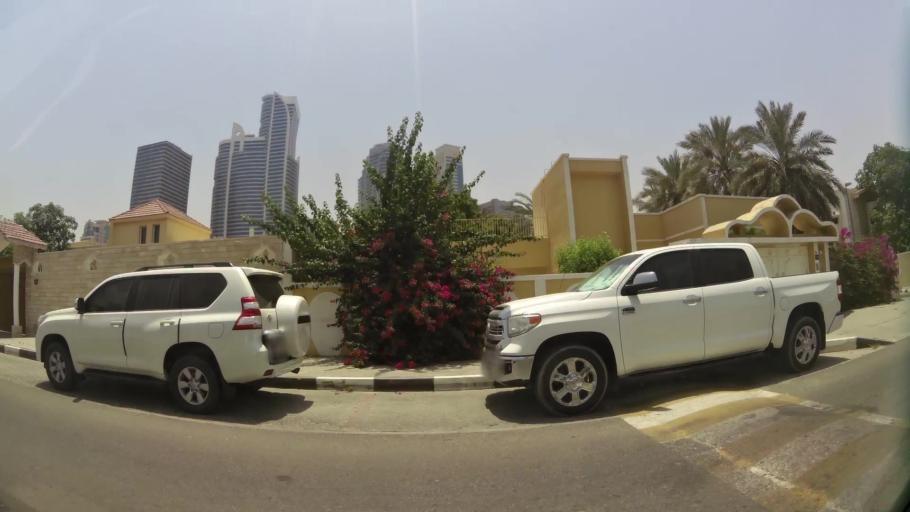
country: AE
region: Ash Shariqah
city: Sharjah
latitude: 25.3367
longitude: 55.3715
